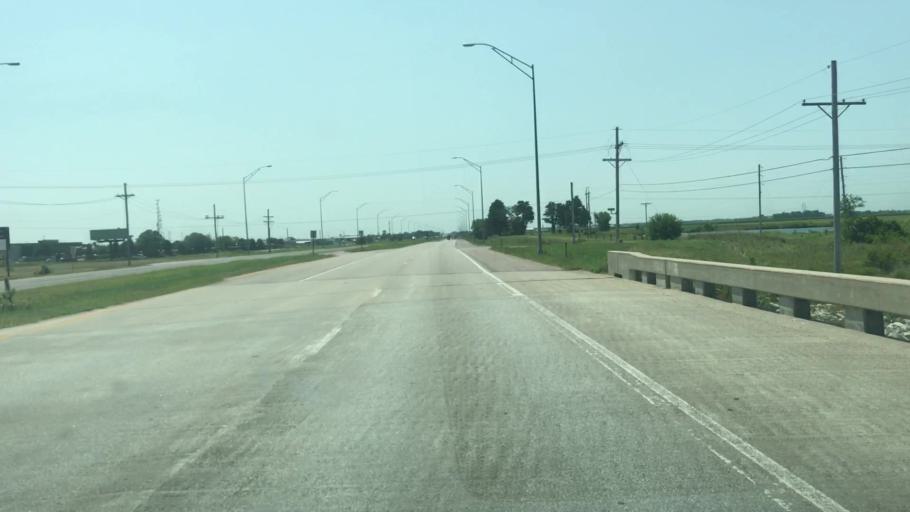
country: US
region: Nebraska
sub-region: Hall County
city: Grand Island
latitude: 40.8744
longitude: -98.3783
